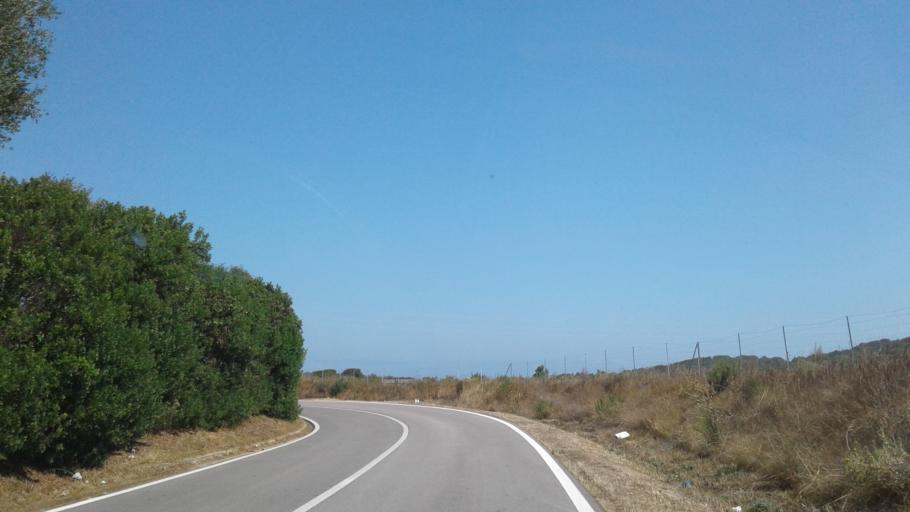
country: IT
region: Sardinia
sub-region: Provincia di Olbia-Tempio
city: Palau
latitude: 41.1601
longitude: 9.3140
